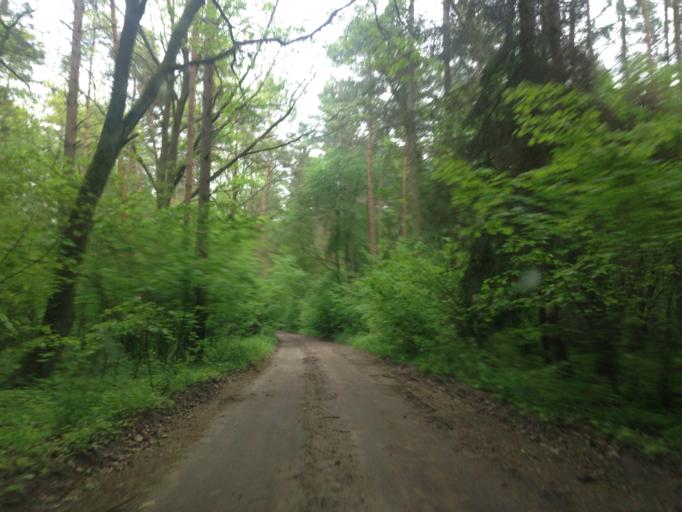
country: PL
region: Kujawsko-Pomorskie
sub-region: Powiat brodnicki
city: Bartniczka
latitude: 53.2695
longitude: 19.5360
